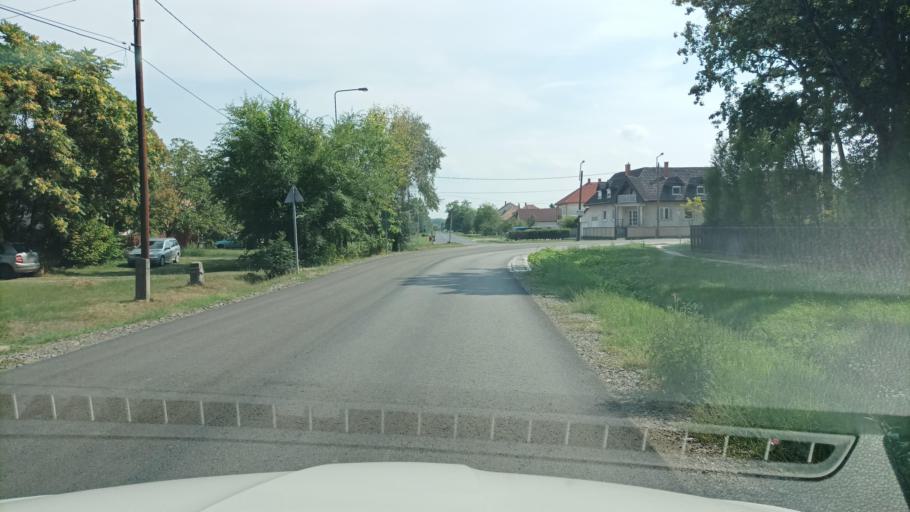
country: HU
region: Pest
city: Tura
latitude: 47.6048
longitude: 19.6051
